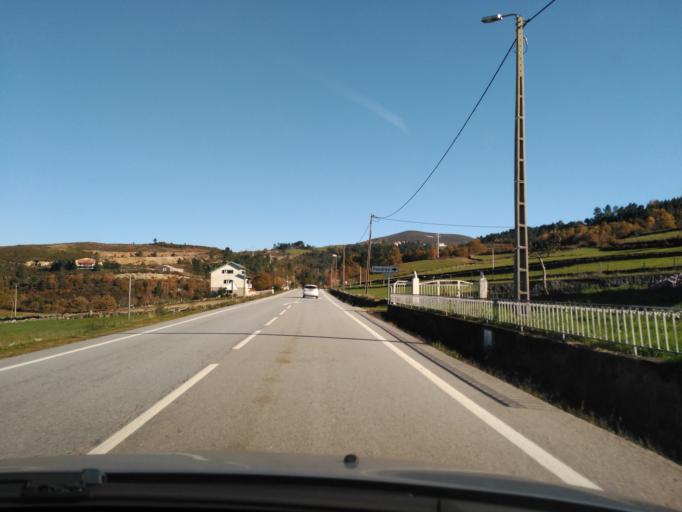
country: PT
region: Vila Real
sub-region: Montalegre
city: Montalegre
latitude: 41.7002
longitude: -7.9307
